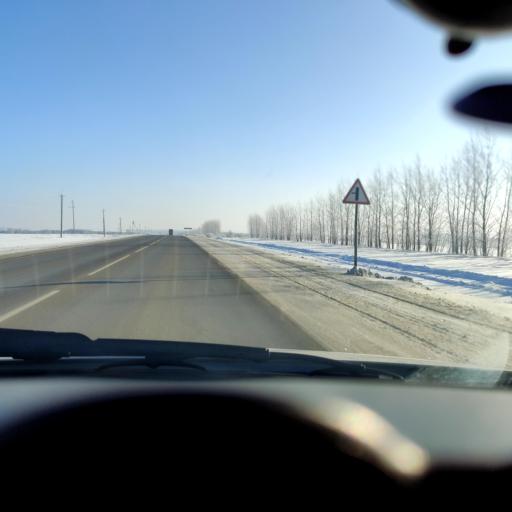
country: RU
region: Kursk
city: Tim
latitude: 51.6540
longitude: 36.9329
